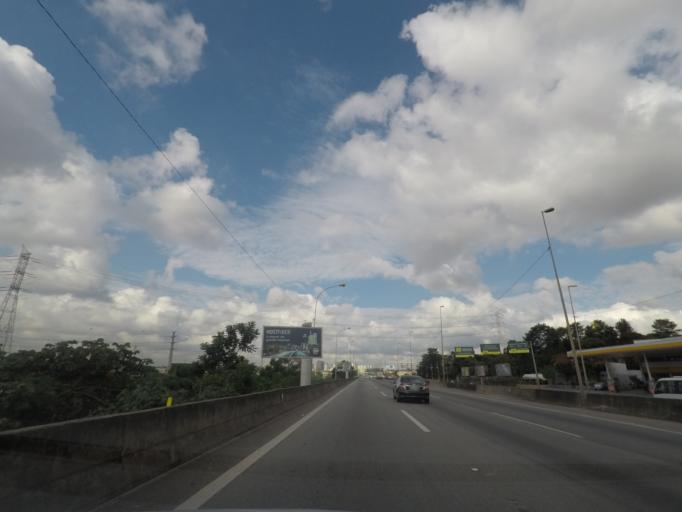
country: BR
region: Sao Paulo
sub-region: Osasco
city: Osasco
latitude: -23.5232
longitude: -46.7625
